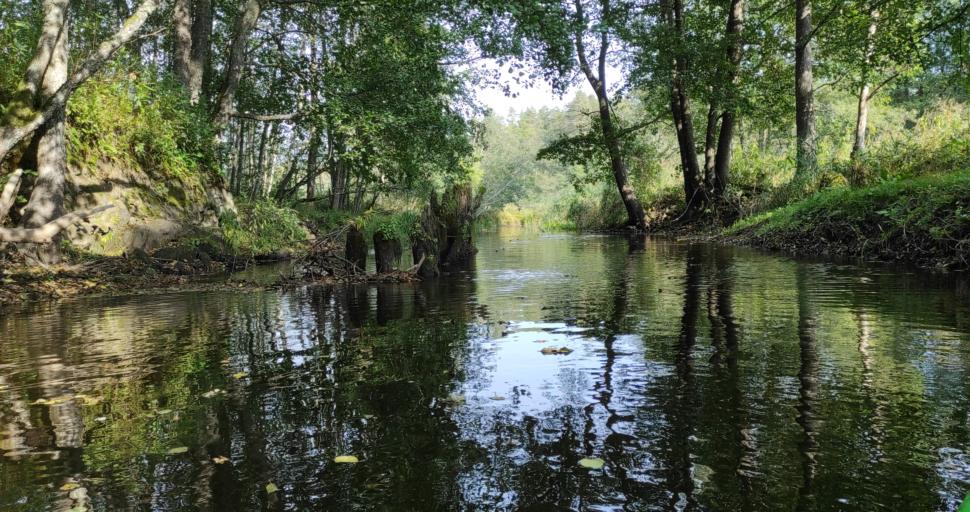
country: LV
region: Kuldigas Rajons
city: Kuldiga
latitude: 57.2653
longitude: 22.0833
